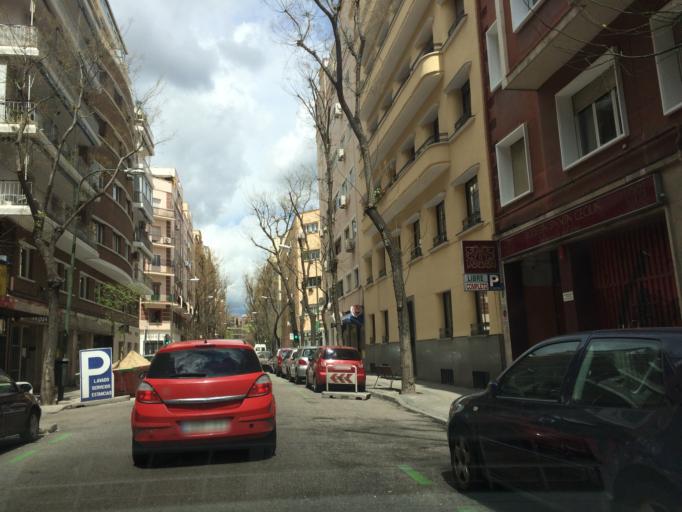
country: ES
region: Madrid
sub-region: Provincia de Madrid
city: Chamberi
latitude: 40.4370
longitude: -3.7113
